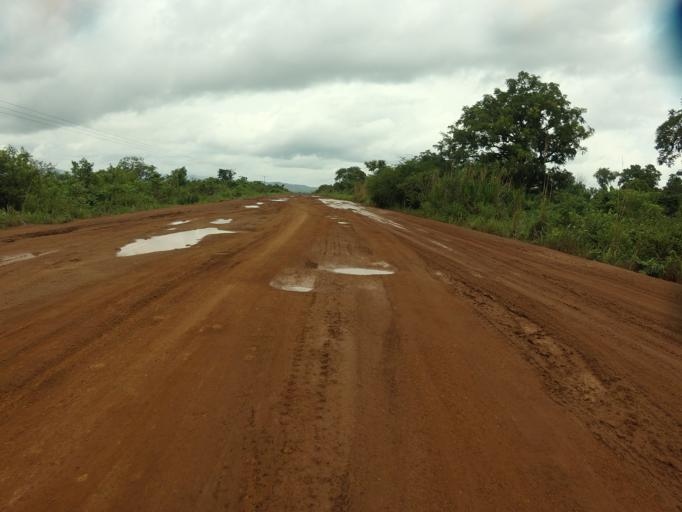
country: GH
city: Kpandae
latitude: 8.3074
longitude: 0.4844
